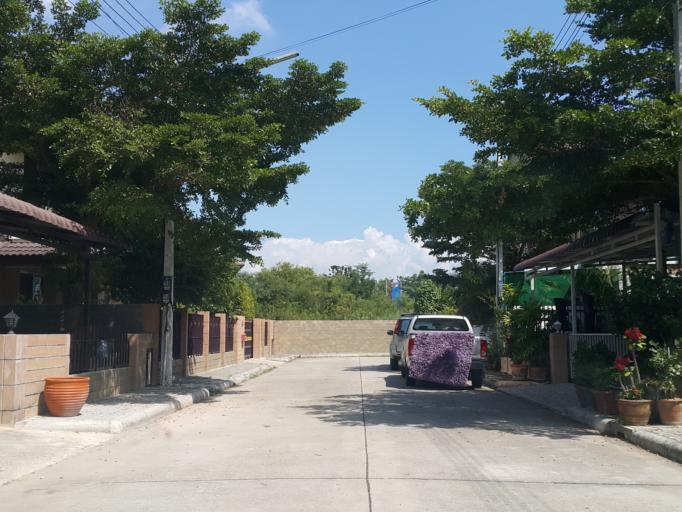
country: TH
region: Chiang Mai
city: Saraphi
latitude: 18.7568
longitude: 99.0573
